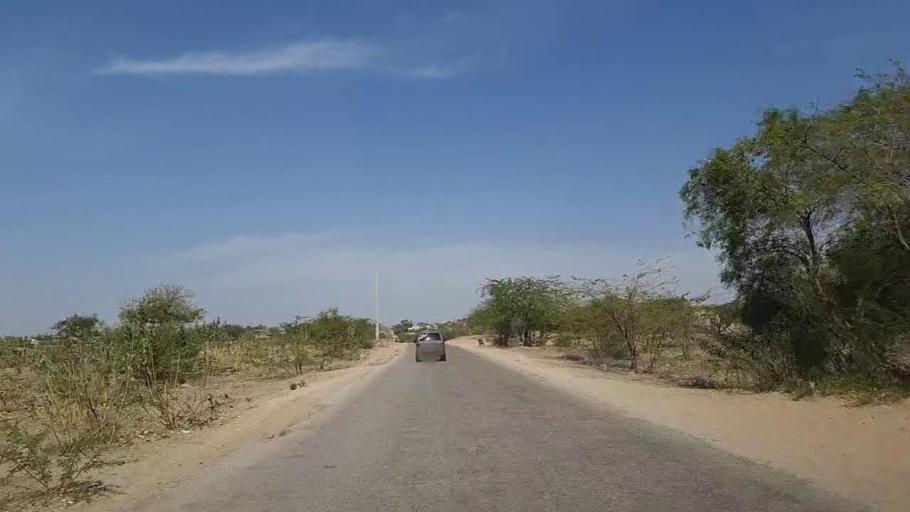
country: PK
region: Sindh
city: Mithi
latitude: 24.9832
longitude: 69.9225
